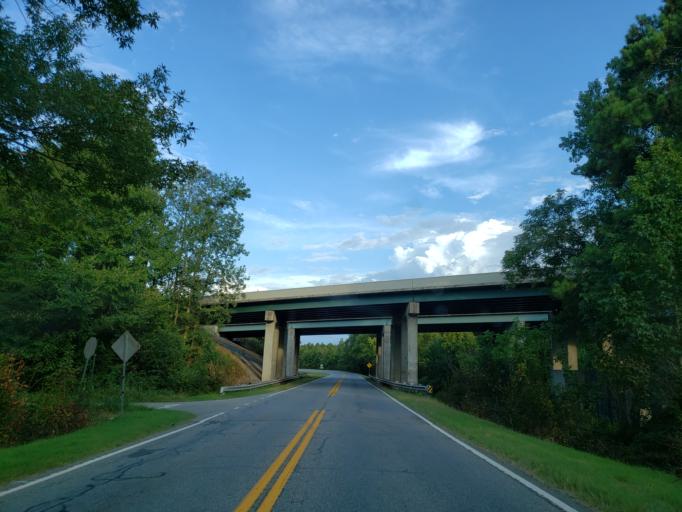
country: US
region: Georgia
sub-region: Bartow County
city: Cartersville
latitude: 34.2199
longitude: -84.8542
